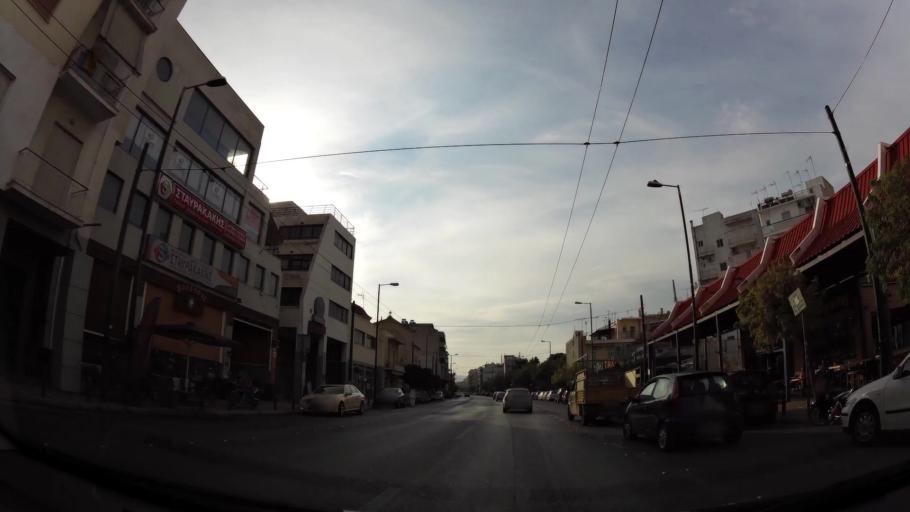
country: GR
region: Attica
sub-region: Nomarchia Athinas
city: Athens
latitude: 37.9935
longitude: 23.7134
